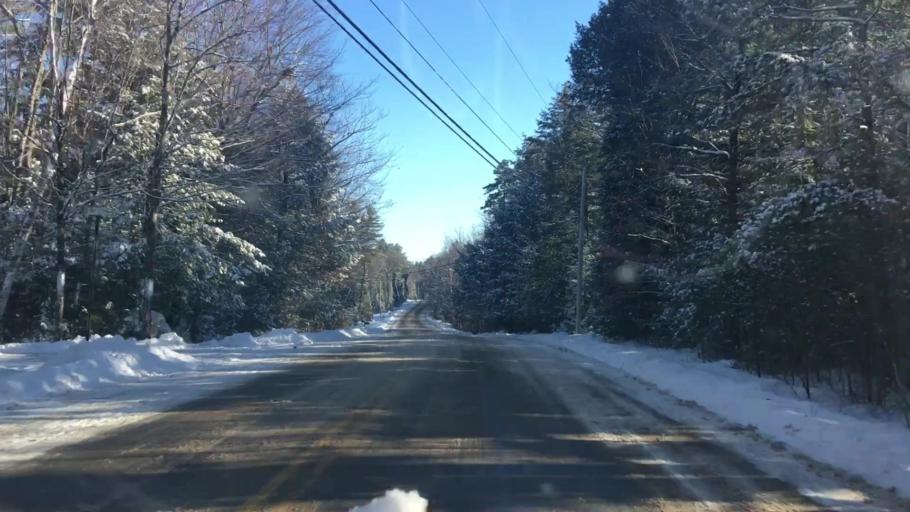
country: US
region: Maine
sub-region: Cumberland County
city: New Gloucester
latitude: 43.9537
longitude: -70.3128
